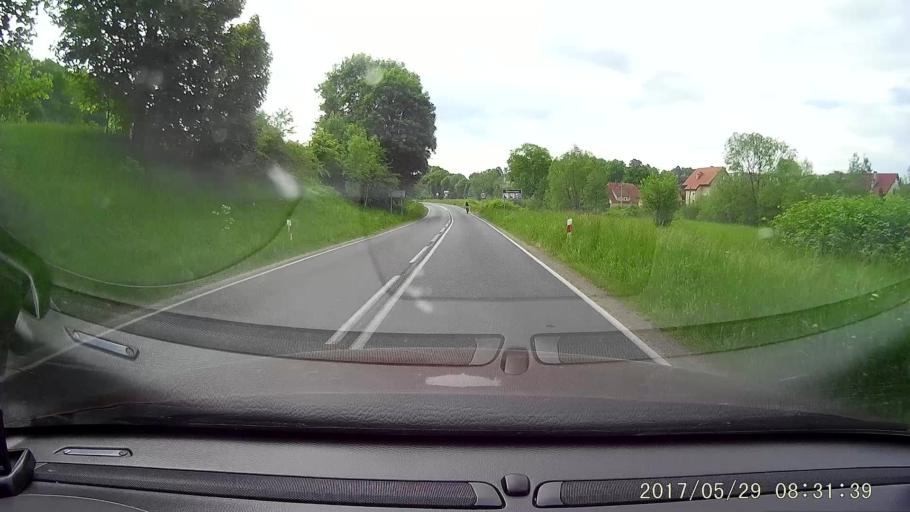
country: PL
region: Lower Silesian Voivodeship
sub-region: Powiat zlotoryjski
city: Swierzawa
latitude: 51.0208
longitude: 15.8839
